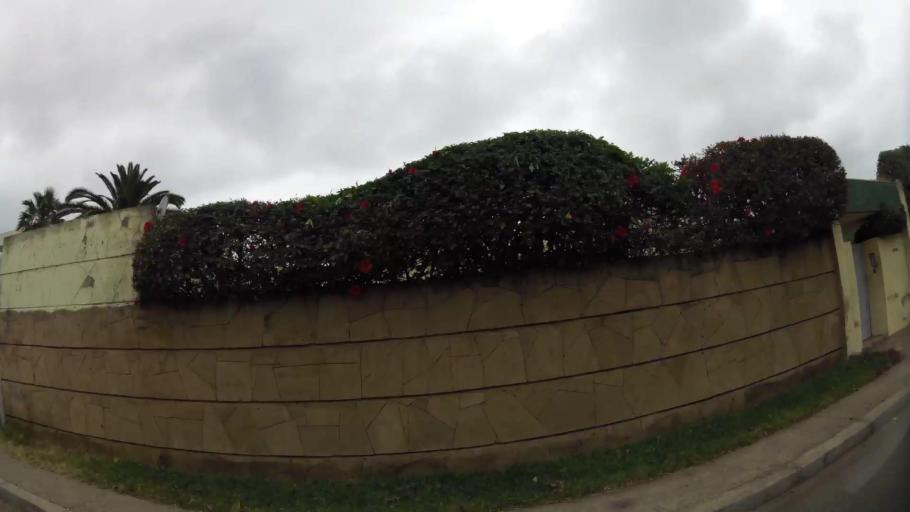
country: MA
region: Rabat-Sale-Zemmour-Zaer
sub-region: Rabat
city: Rabat
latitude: 33.9753
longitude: -6.8279
